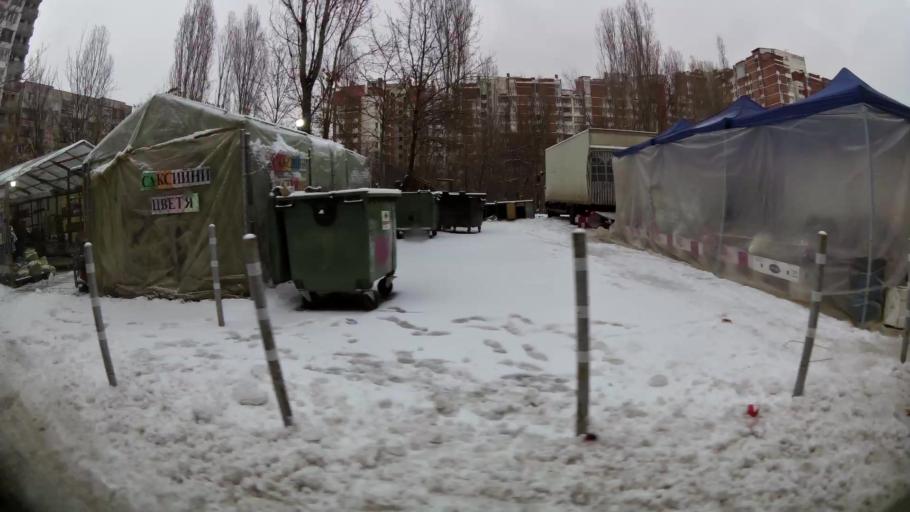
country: BG
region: Sofia-Capital
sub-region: Stolichna Obshtina
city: Sofia
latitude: 42.7041
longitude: 23.3017
